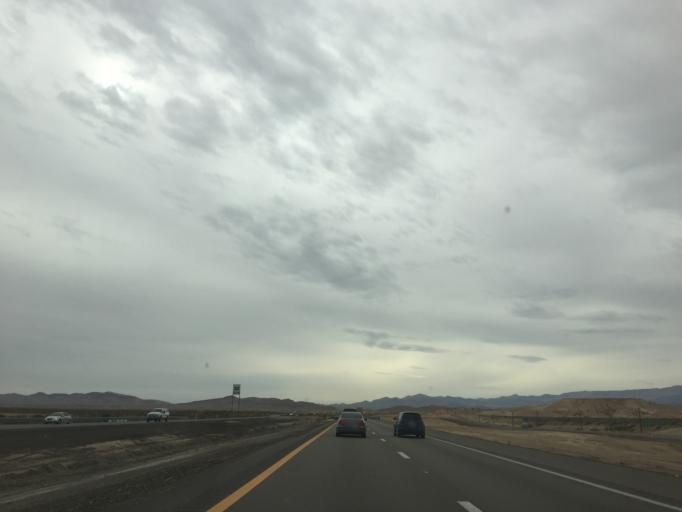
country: US
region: Nevada
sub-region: Clark County
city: Moapa Town
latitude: 36.5040
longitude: -114.7585
